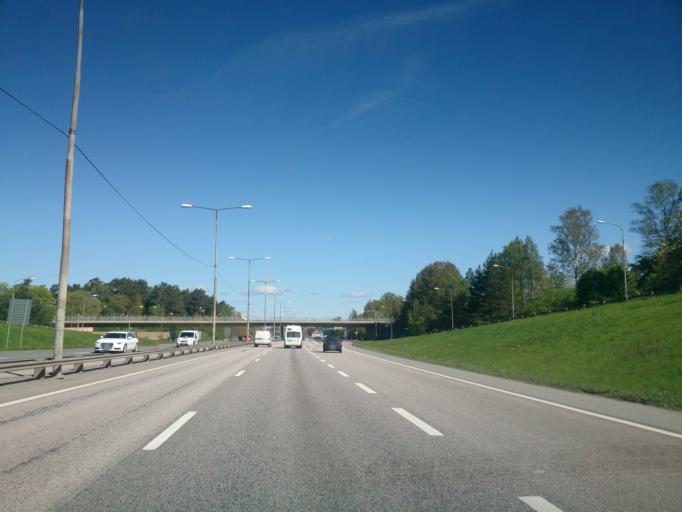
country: SE
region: Stockholm
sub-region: Stockholms Kommun
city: Arsta
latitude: 59.2731
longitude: 18.0939
